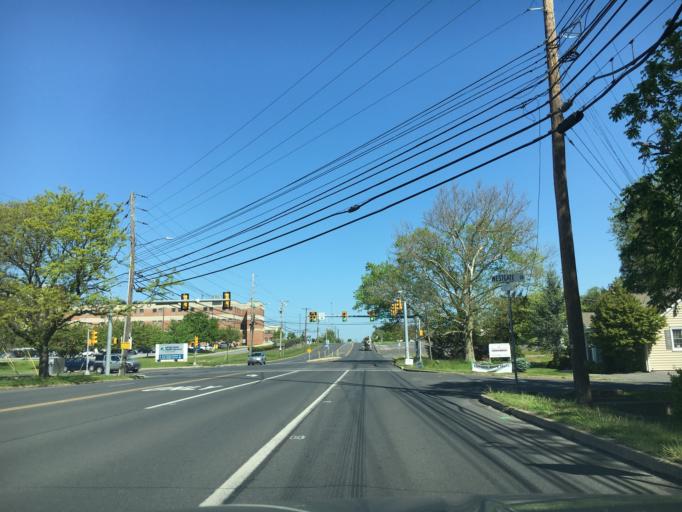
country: US
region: Pennsylvania
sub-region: Northampton County
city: Bethlehem
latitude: 40.6441
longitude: -75.4042
